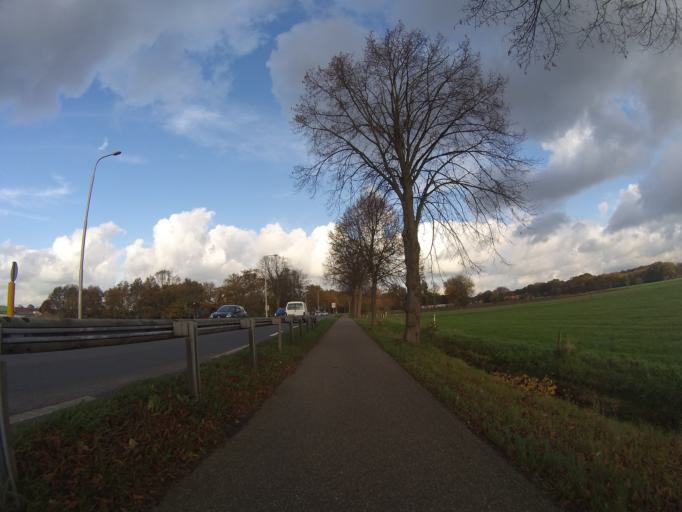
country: NL
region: Utrecht
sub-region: Gemeente Amersfoort
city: Randenbroek
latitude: 52.1791
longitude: 5.4362
